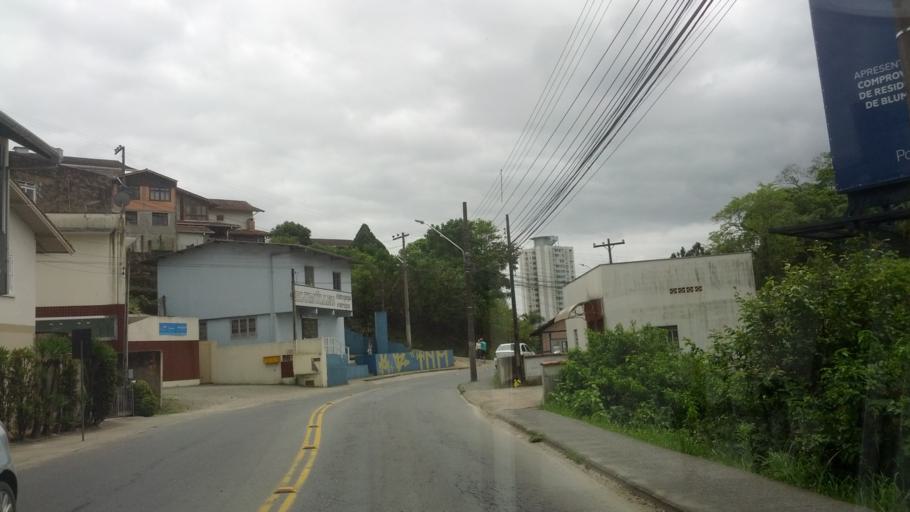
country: BR
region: Santa Catarina
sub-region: Blumenau
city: Blumenau
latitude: -26.9084
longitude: -49.0919
